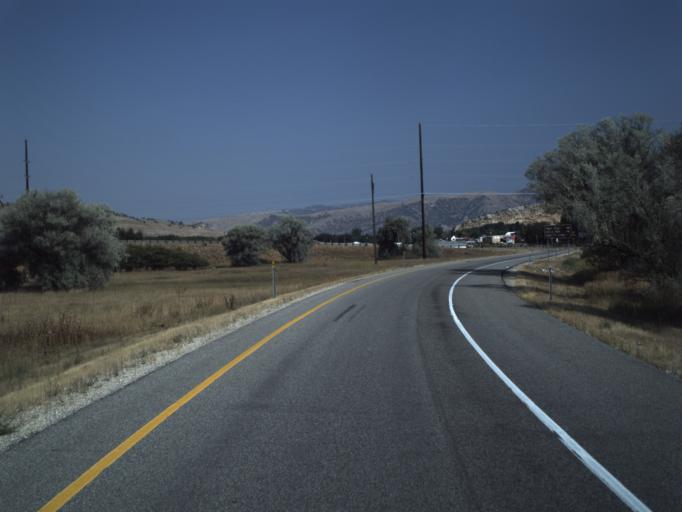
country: US
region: Utah
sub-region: Summit County
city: Coalville
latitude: 40.9106
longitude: -111.4006
